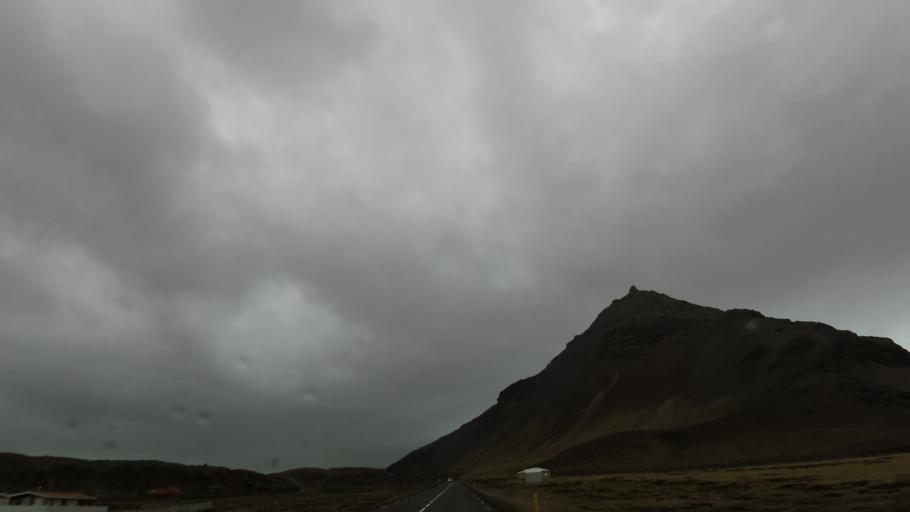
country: IS
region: West
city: Olafsvik
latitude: 64.7665
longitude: -23.6370
